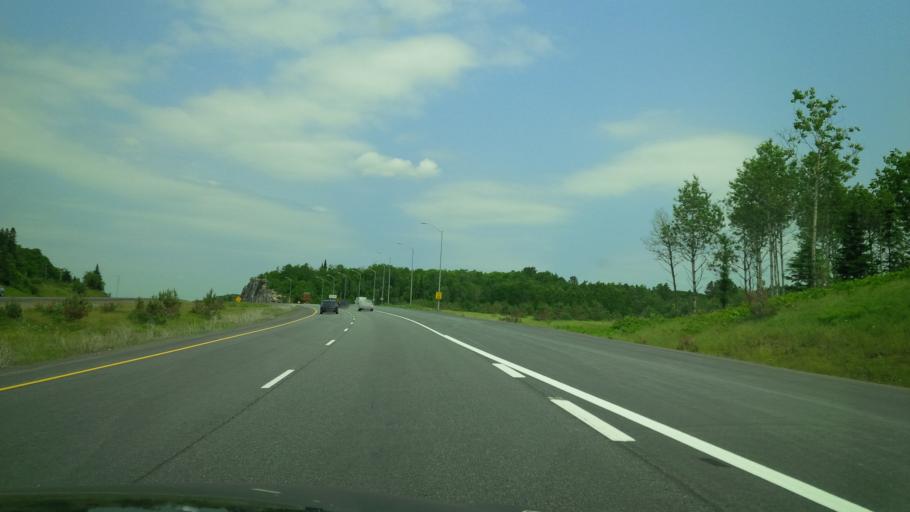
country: CA
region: Ontario
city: Huntsville
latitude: 45.4189
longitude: -79.2374
